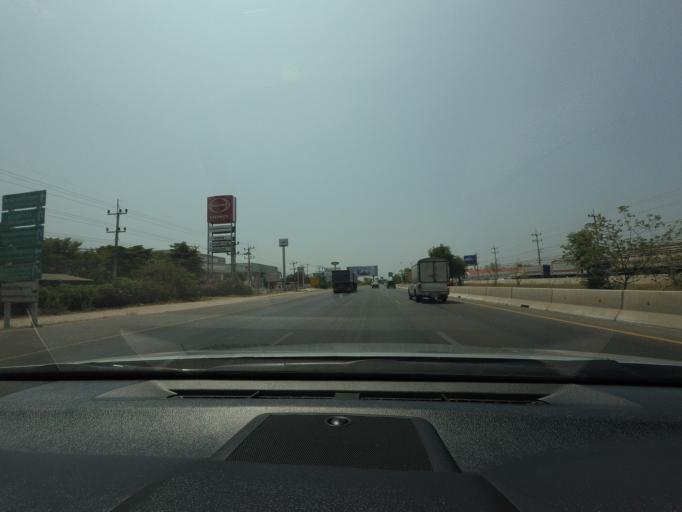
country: TH
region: Samut Songkhram
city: Samut Songkhram
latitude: 13.4130
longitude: 100.0259
